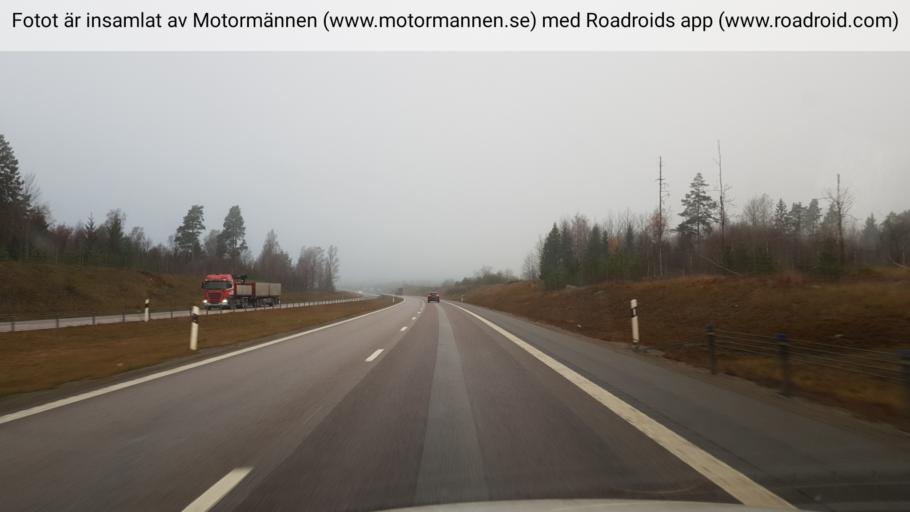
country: SE
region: Uppsala
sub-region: Tierps Kommun
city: Tierp
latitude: 60.3159
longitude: 17.5195
